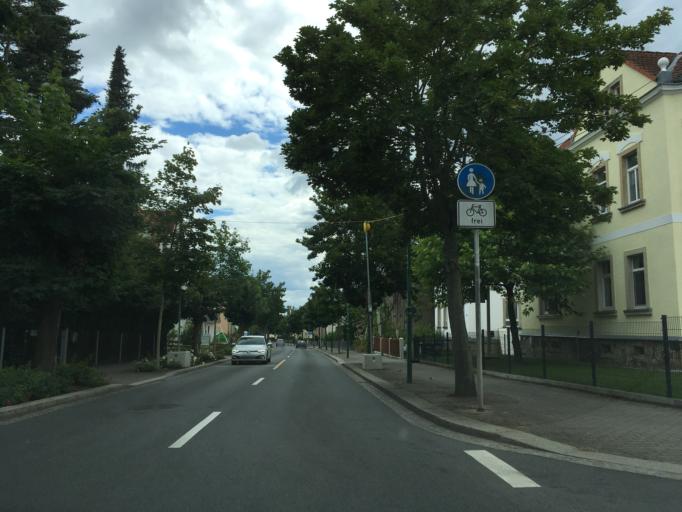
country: DE
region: Saxony
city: Radeberg
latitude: 51.1267
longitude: 13.9164
